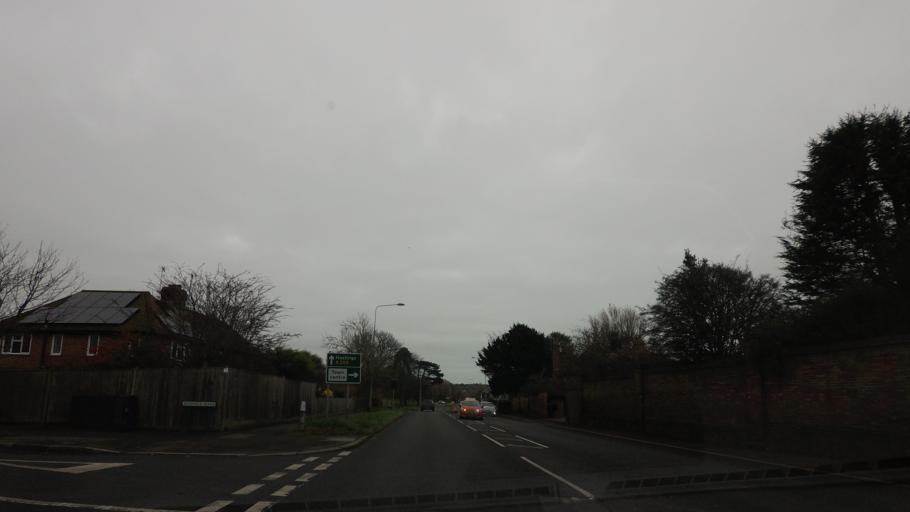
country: GB
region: England
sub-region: East Sussex
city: Bexhill-on-Sea
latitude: 50.8464
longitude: 0.4555
